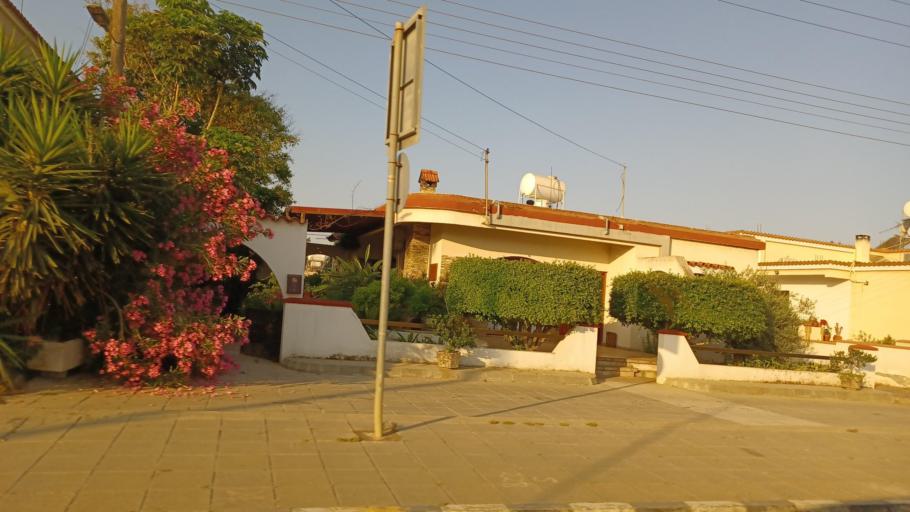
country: CY
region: Larnaka
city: Xylotymbou
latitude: 35.0328
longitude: 33.7641
